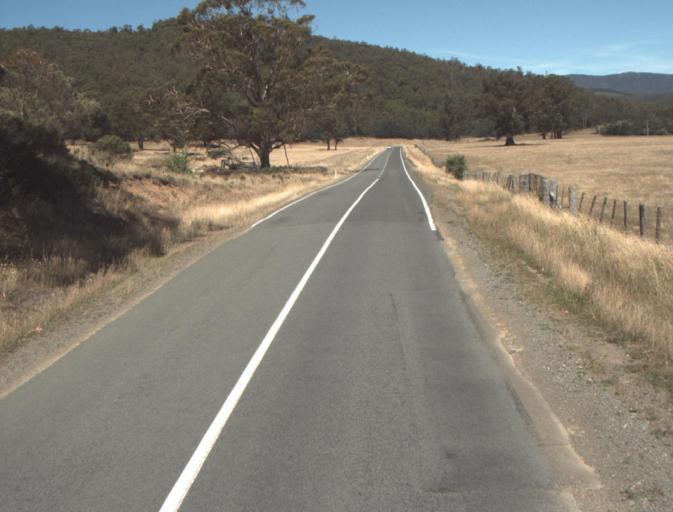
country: AU
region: Tasmania
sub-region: Dorset
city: Scottsdale
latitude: -41.2884
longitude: 147.3845
